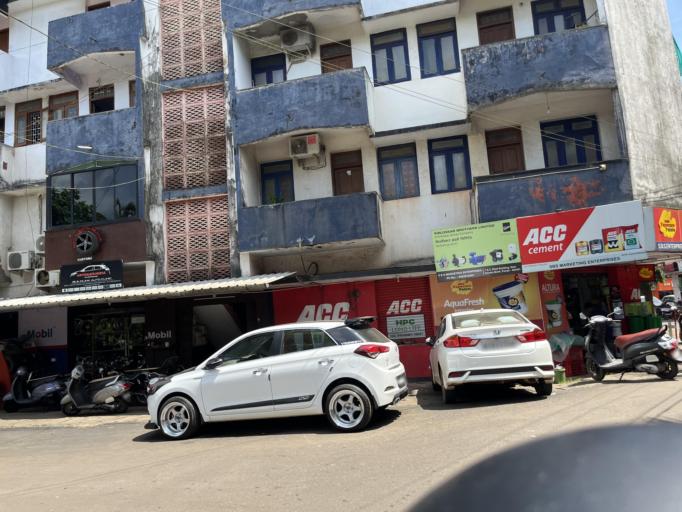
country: IN
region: Goa
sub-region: North Goa
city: Ponda
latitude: 15.4019
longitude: 74.0056
